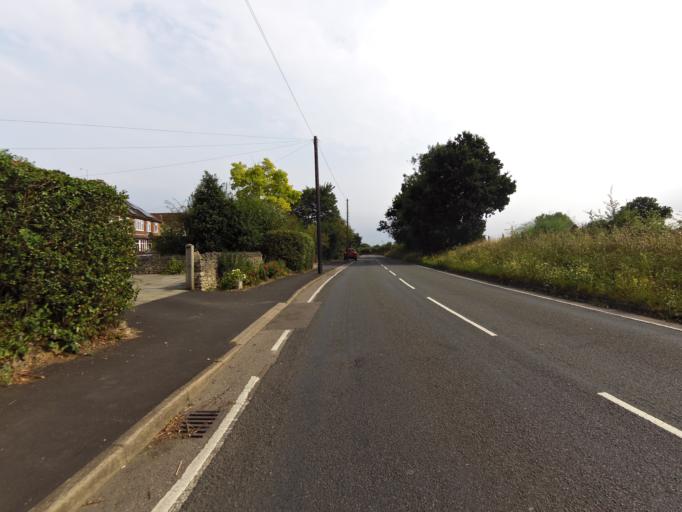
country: GB
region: England
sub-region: Hertfordshire
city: St Albans
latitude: 51.7473
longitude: -0.2832
